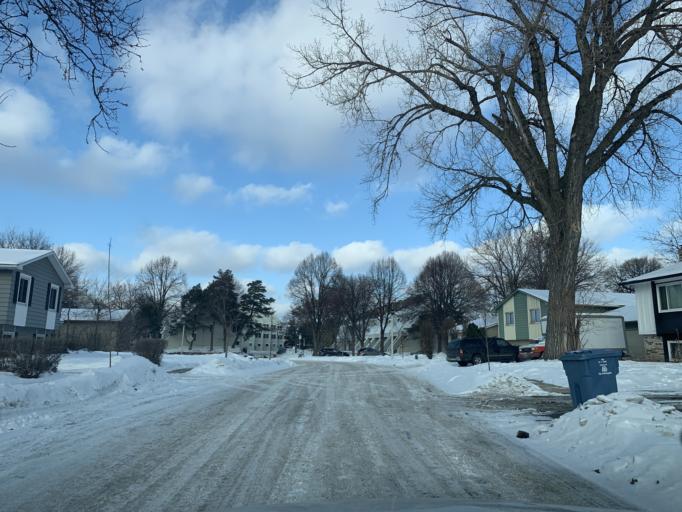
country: US
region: Minnesota
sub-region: Hennepin County
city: Minneapolis
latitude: 44.9967
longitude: -93.2850
